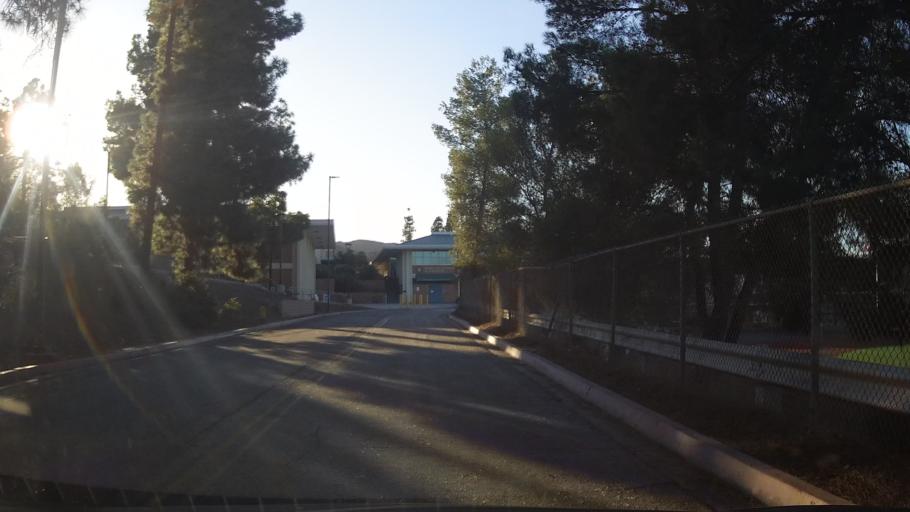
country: US
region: California
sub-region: San Diego County
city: Santee
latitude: 32.8176
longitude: -117.0048
